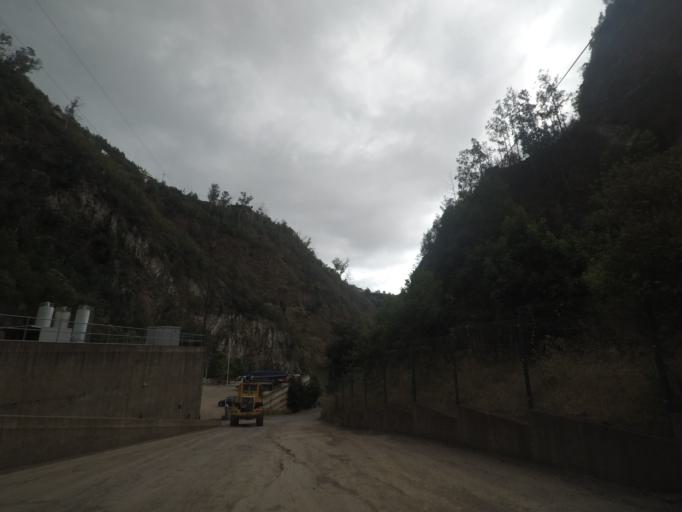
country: PT
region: Madeira
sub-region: Funchal
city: Nossa Senhora do Monte
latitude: 32.6850
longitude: -16.9155
